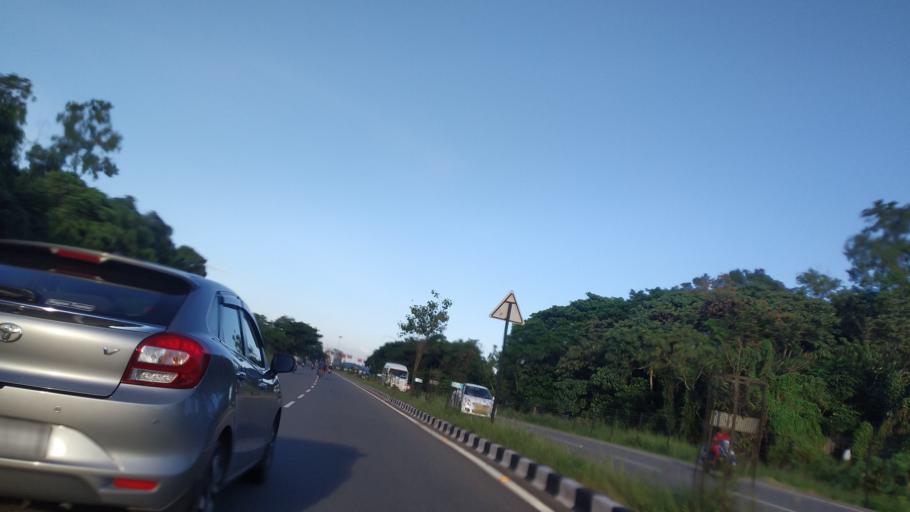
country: IN
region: Kerala
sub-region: Ernakulam
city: Elur
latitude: 10.0693
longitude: 76.3142
